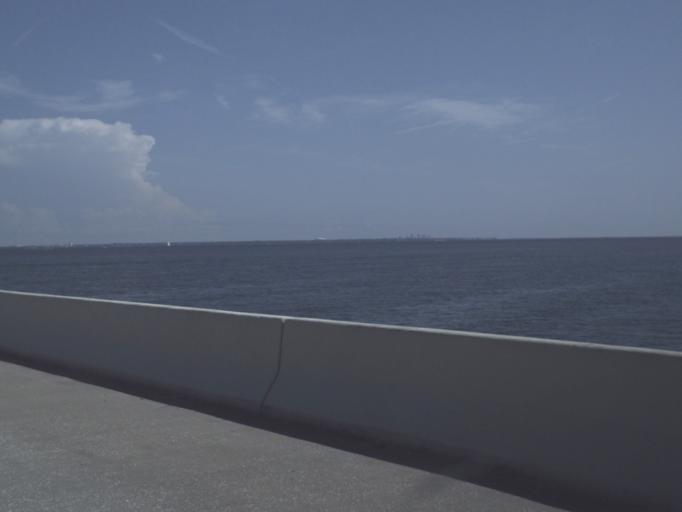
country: US
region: Florida
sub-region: Manatee County
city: West Bradenton
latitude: 27.6022
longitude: -82.6415
